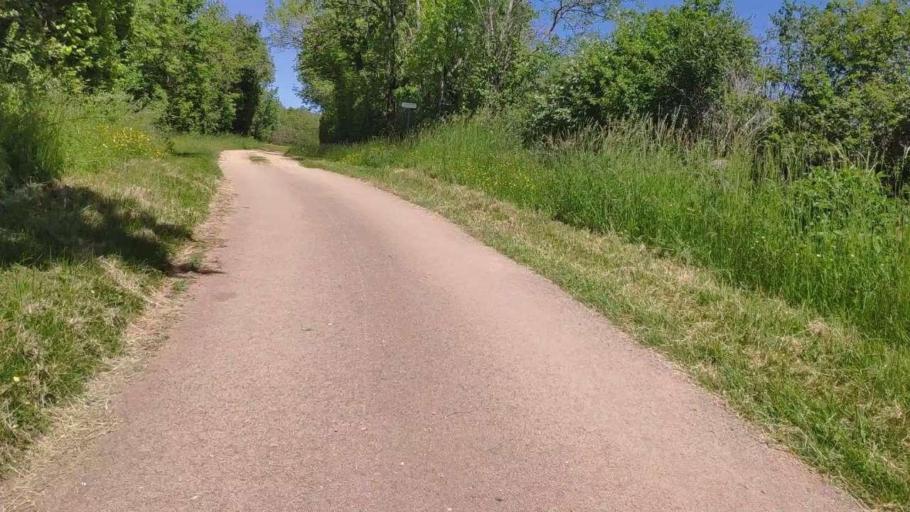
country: FR
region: Franche-Comte
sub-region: Departement du Jura
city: Perrigny
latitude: 46.7244
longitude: 5.6458
